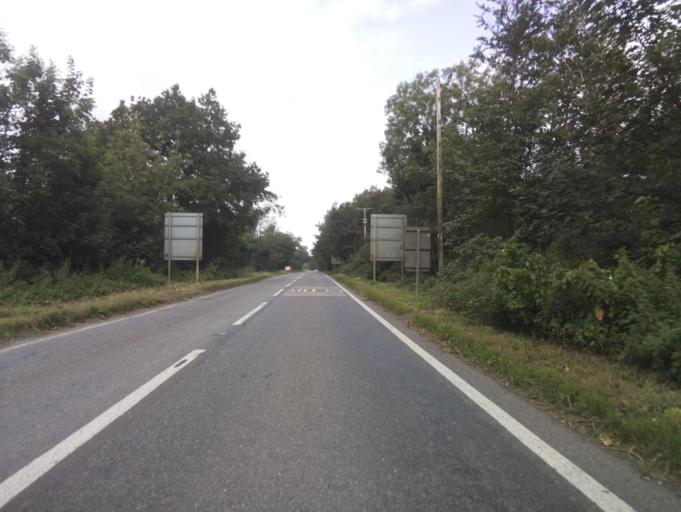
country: GB
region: England
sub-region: Somerset
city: Shepton Mallet
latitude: 51.2056
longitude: -2.4914
